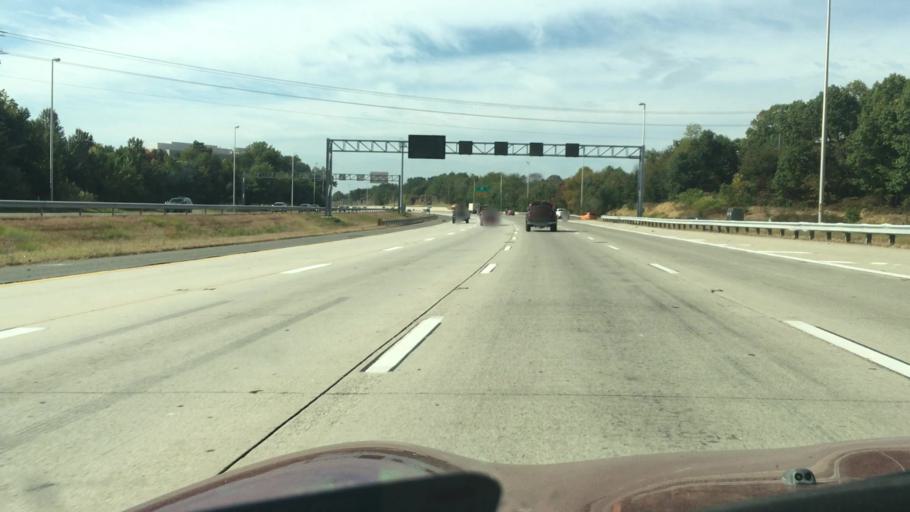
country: US
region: Virginia
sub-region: Fairfax County
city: Centreville
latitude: 38.8464
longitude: -77.4339
